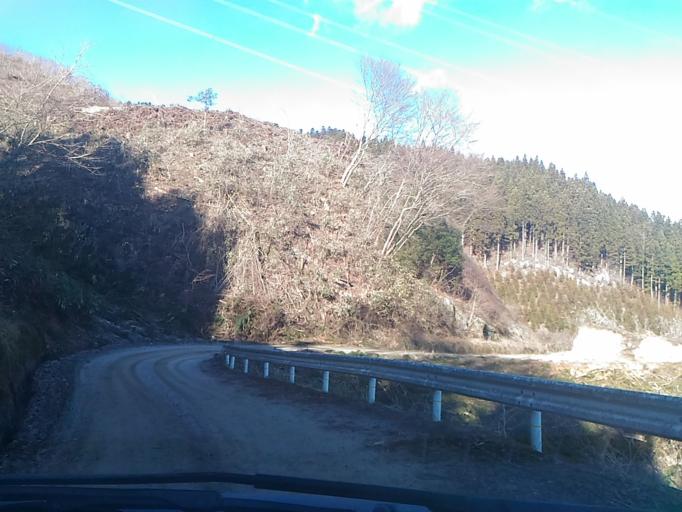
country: JP
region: Fukushima
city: Ishikawa
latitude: 37.0436
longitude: 140.6002
